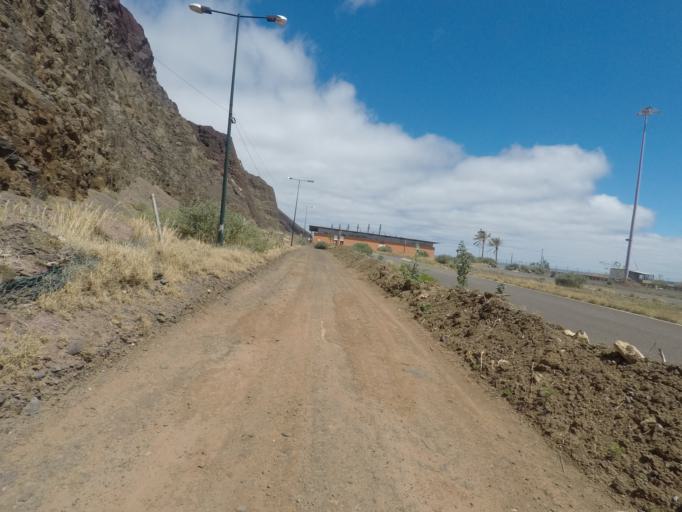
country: PT
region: Madeira
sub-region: Porto Santo
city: Vila de Porto Santo
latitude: 33.0641
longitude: -16.3086
